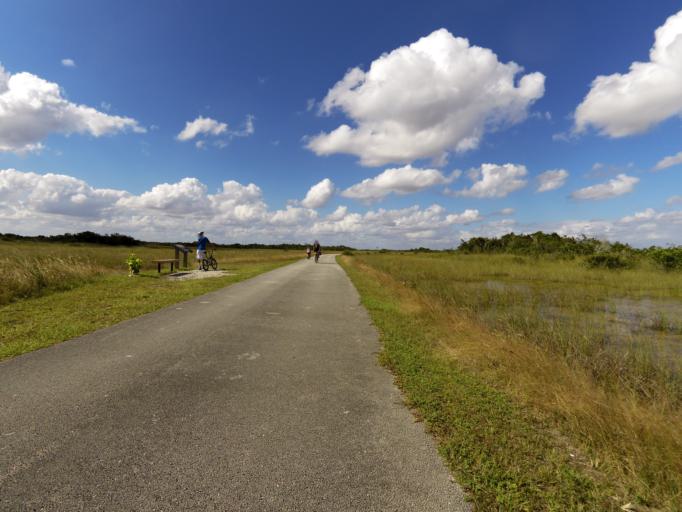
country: US
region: Florida
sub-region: Miami-Dade County
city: The Hammocks
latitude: 25.7059
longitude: -80.7614
